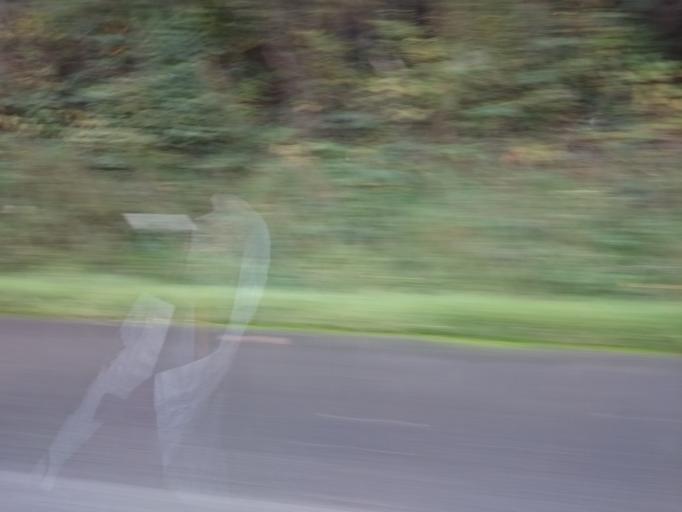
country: FR
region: Brittany
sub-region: Departement des Cotes-d'Armor
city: Pedernec
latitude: 48.5689
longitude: -3.2885
